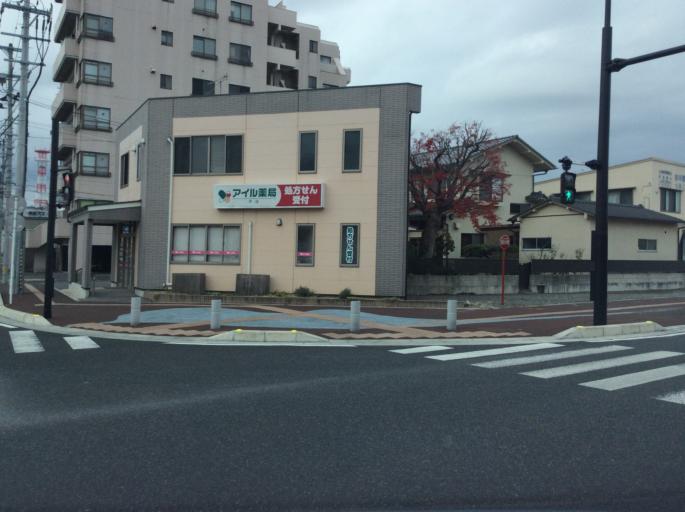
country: JP
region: Fukushima
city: Iwaki
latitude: 37.0512
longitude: 140.8972
